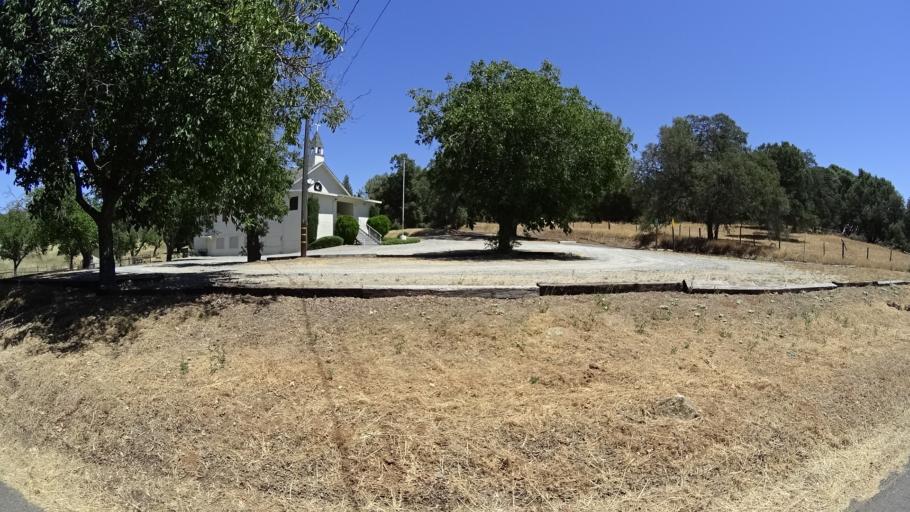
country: US
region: California
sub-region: Calaveras County
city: Mountain Ranch
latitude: 38.2313
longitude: -120.5477
